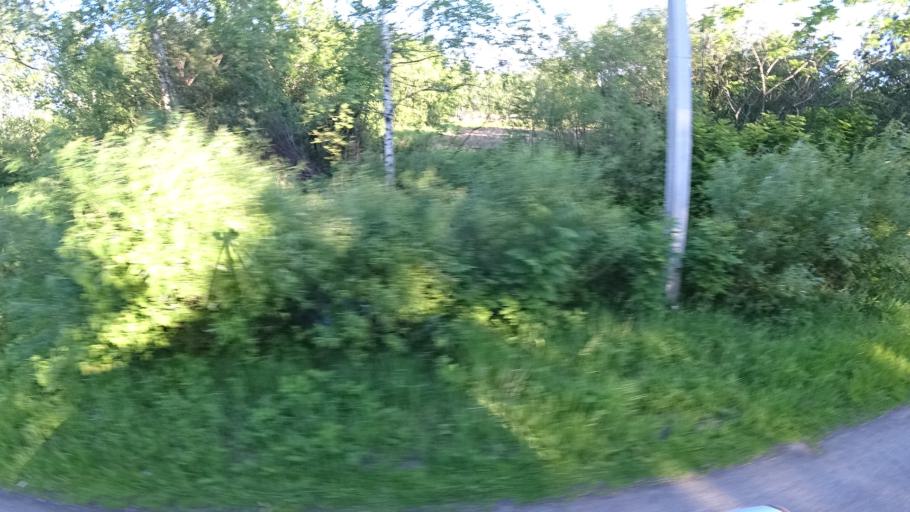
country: RU
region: Khabarovsk Krai
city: Khor
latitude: 47.8539
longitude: 134.9836
